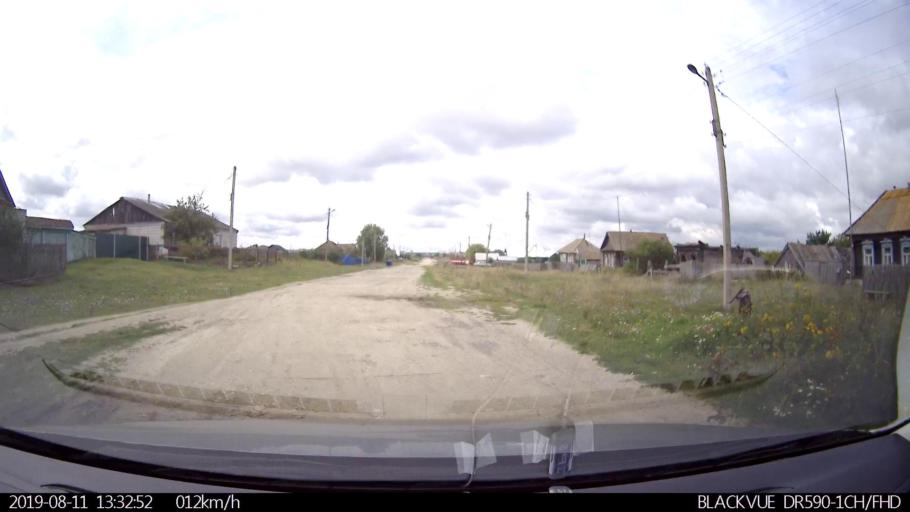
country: RU
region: Ulyanovsk
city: Ignatovka
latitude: 53.8592
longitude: 47.5968
